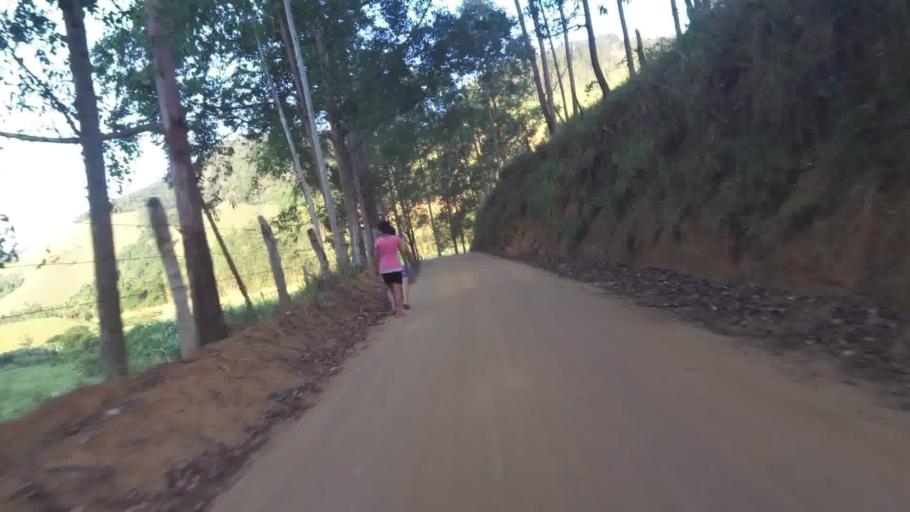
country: BR
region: Espirito Santo
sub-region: Alfredo Chaves
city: Alfredo Chaves
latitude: -20.6103
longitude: -40.7194
